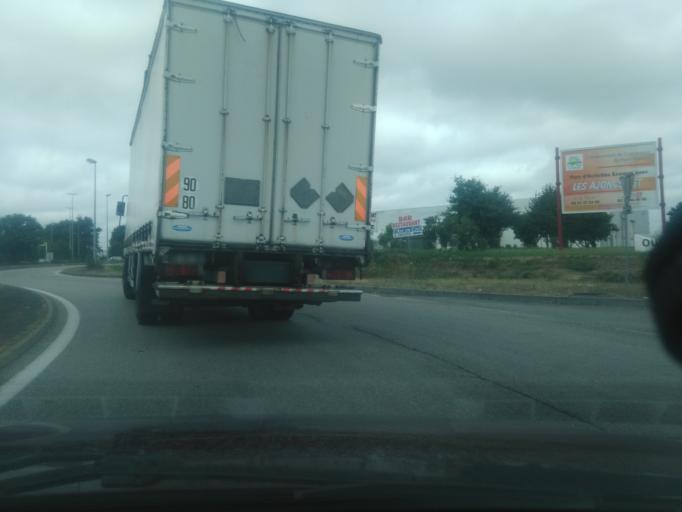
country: FR
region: Pays de la Loire
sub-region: Departement de la Vendee
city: Dompierre-sur-Yon
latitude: 46.6939
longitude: -1.3631
